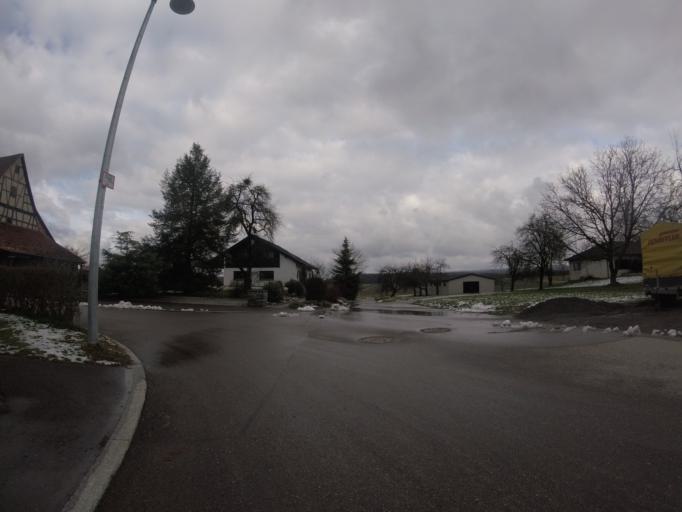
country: DE
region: Baden-Wuerttemberg
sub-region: Regierungsbezirk Stuttgart
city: Aspach
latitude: 48.9654
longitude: 9.3821
